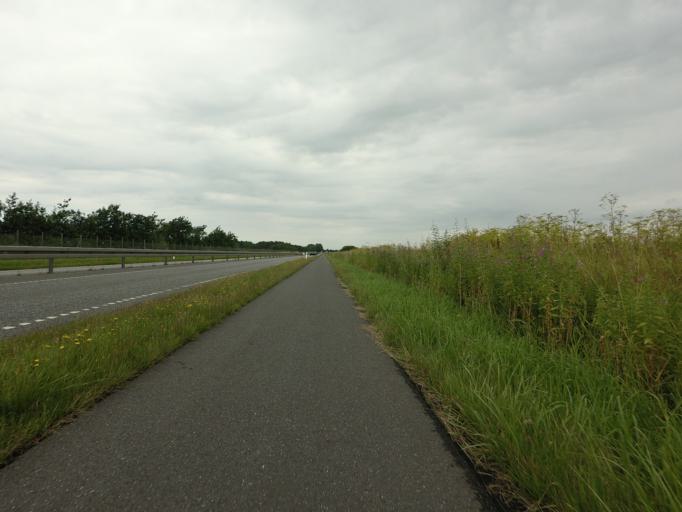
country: DK
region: North Denmark
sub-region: Alborg Kommune
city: Vadum
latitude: 57.0953
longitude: 9.8864
